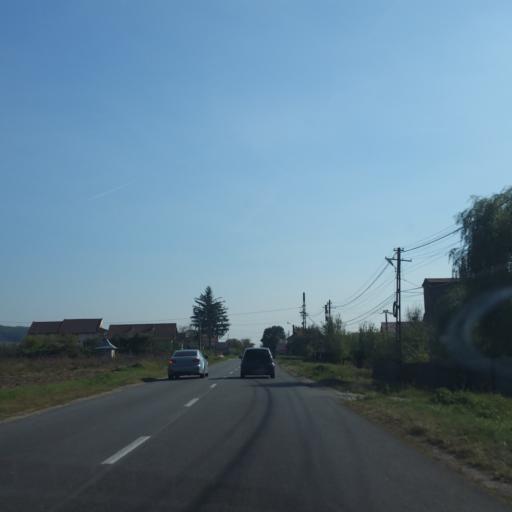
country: RO
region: Arges
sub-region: Comuna Baiculesti
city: Baiculesti
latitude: 45.0665
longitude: 24.6891
